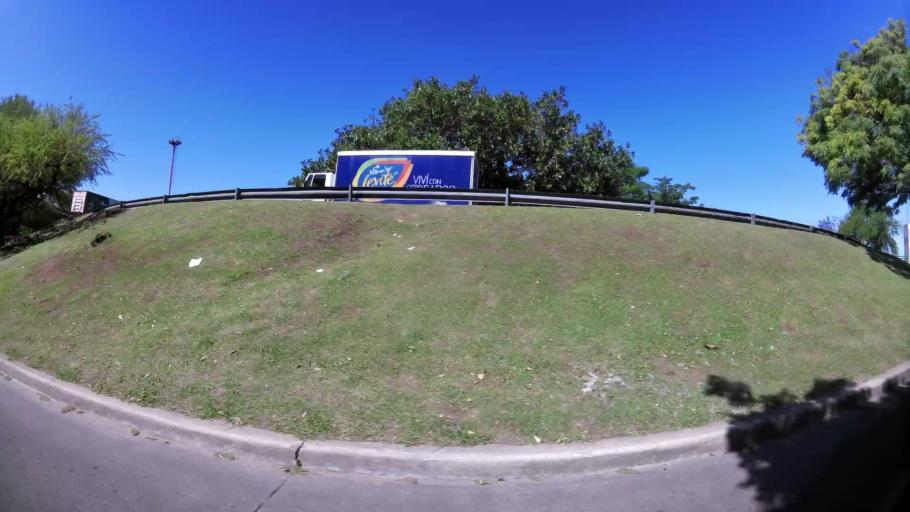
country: AR
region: Santa Fe
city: Santa Fe de la Vera Cruz
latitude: -31.6411
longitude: -60.6845
